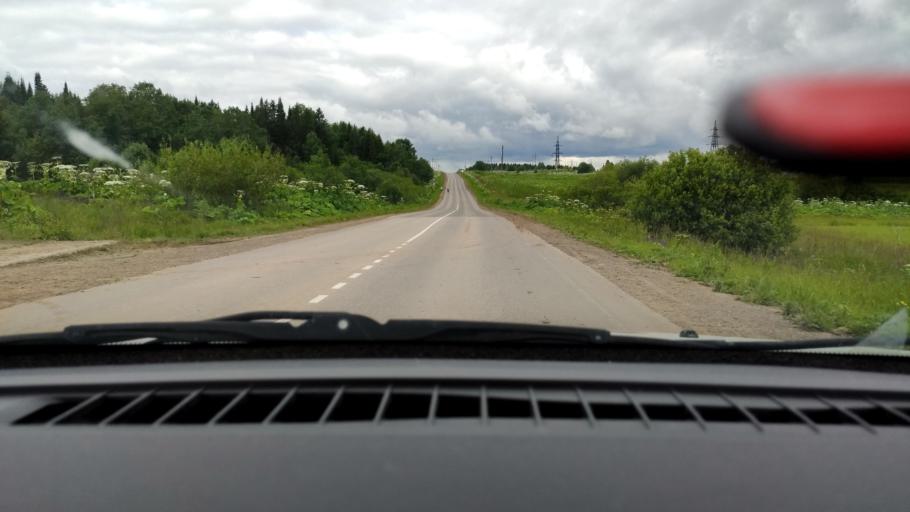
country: RU
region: Perm
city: Chaykovskaya
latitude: 58.1220
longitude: 55.5632
